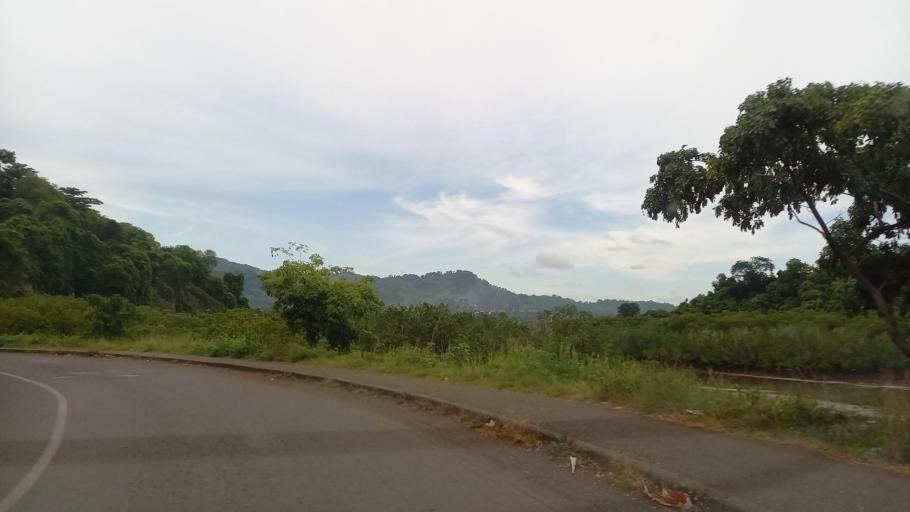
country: YT
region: Mamoudzou
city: Mamoudzou
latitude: -12.7755
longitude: 45.2318
